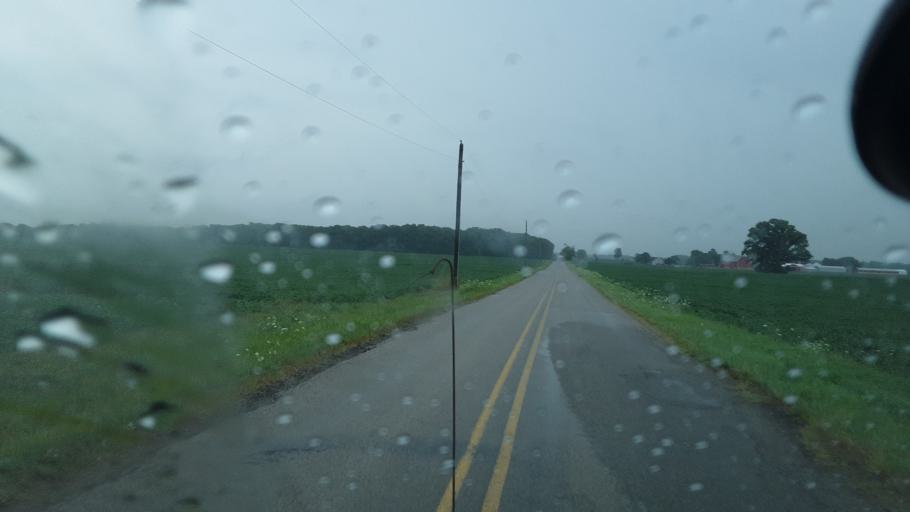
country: US
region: Indiana
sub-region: DeKalb County
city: Butler
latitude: 41.4617
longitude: -84.8140
